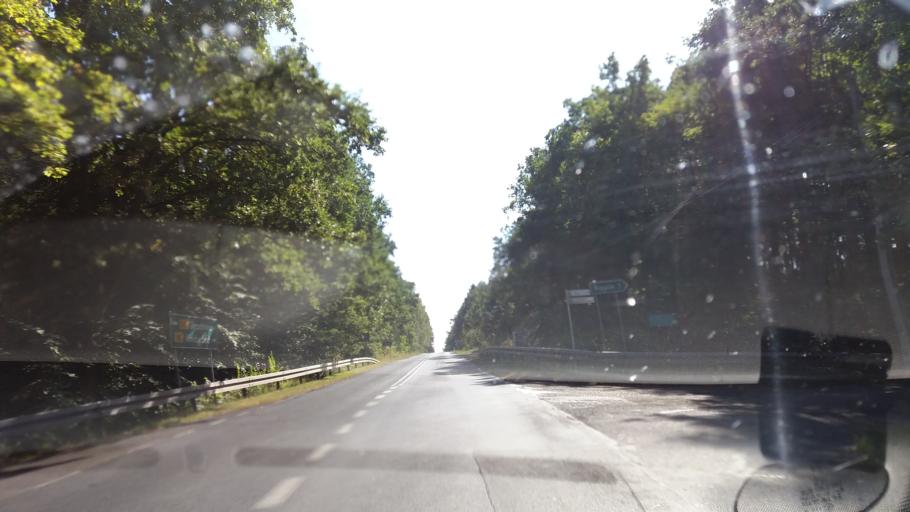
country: PL
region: Lubusz
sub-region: Powiat strzelecko-drezdenecki
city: Drezdenko
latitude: 52.7853
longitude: 15.8393
